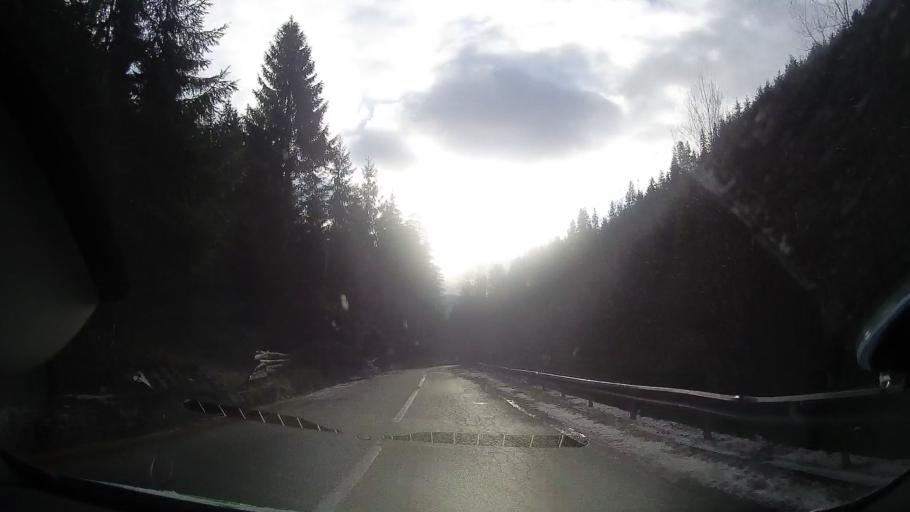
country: RO
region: Alba
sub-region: Comuna Albac
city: Albac
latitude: 46.4723
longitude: 22.9649
